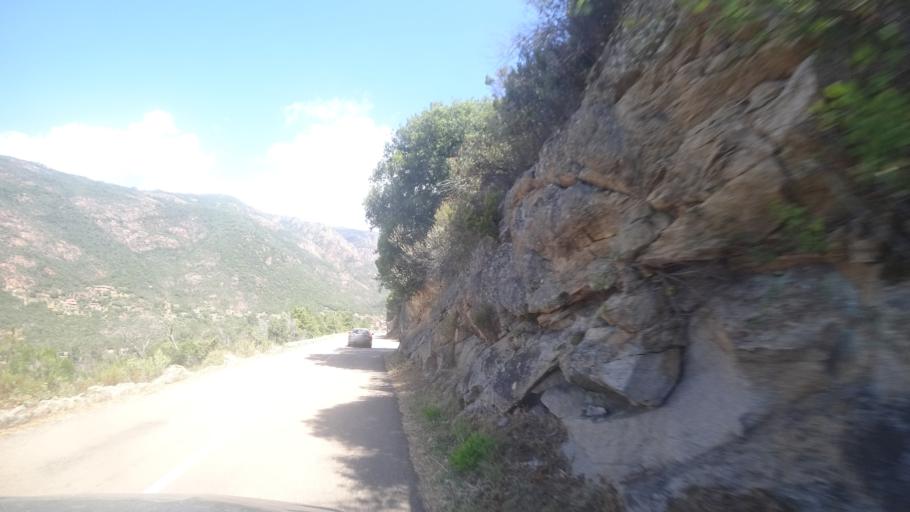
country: FR
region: Corsica
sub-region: Departement de la Corse-du-Sud
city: Cargese
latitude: 42.2626
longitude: 8.6931
